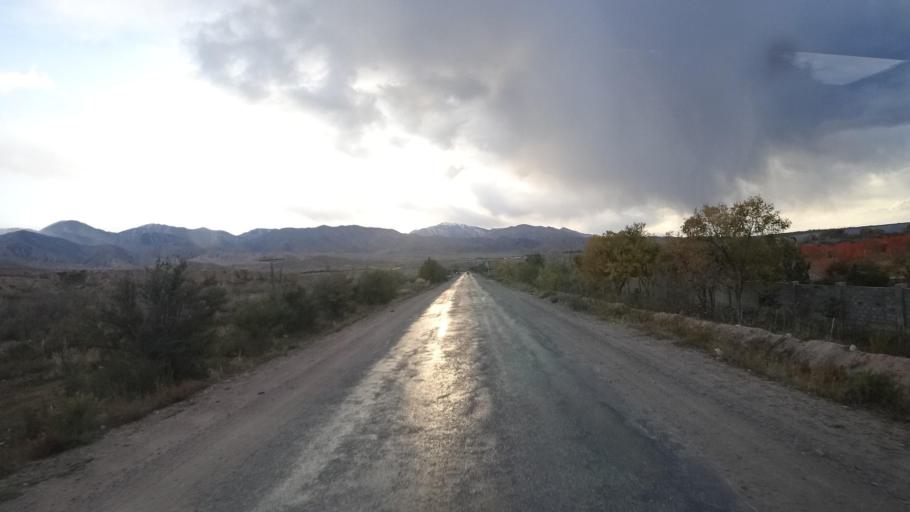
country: KG
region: Ysyk-Koel
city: Kadzhi-Say
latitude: 42.1567
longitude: 77.5085
